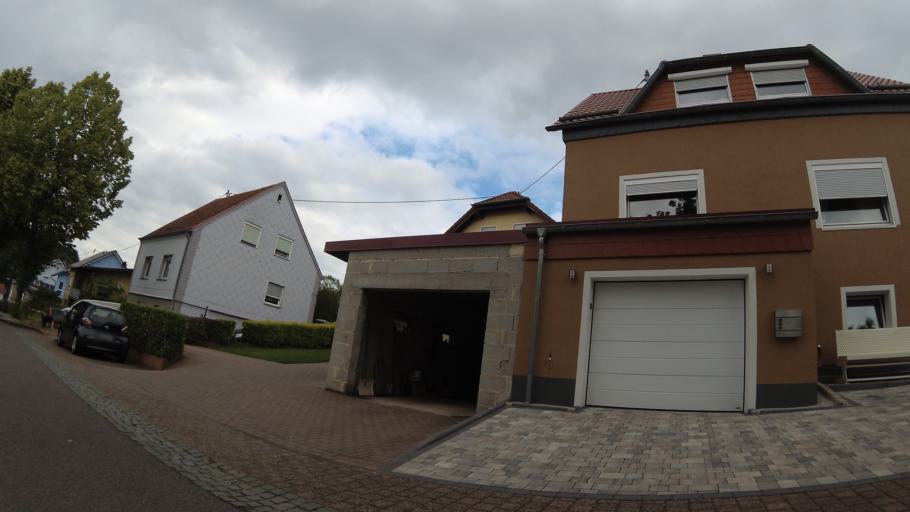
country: DE
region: Saarland
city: Tholey
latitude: 49.4958
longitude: 7.0291
